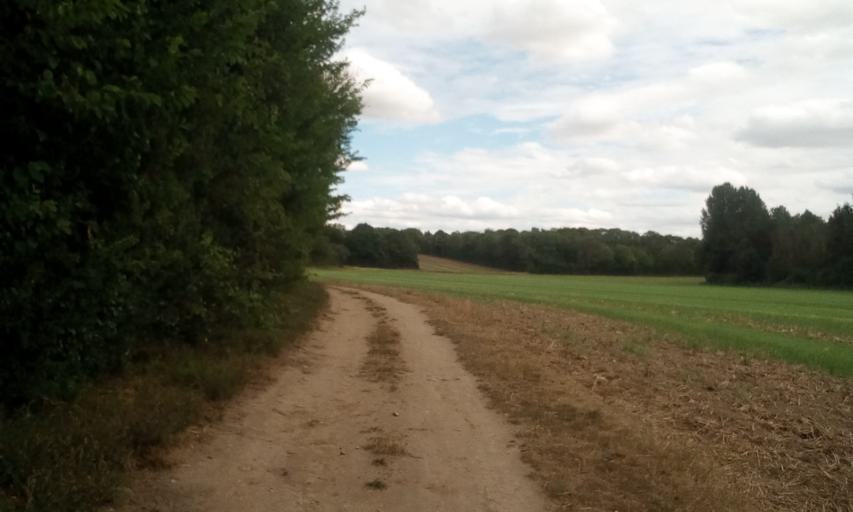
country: FR
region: Lower Normandy
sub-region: Departement du Calvados
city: Bellengreville
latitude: 49.1147
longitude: -0.2004
